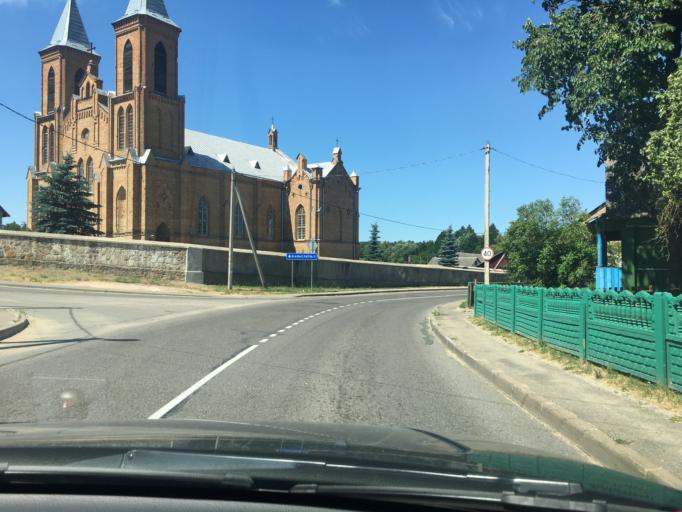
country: BY
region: Grodnenskaya
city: Hal'shany
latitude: 54.1553
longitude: 25.9079
